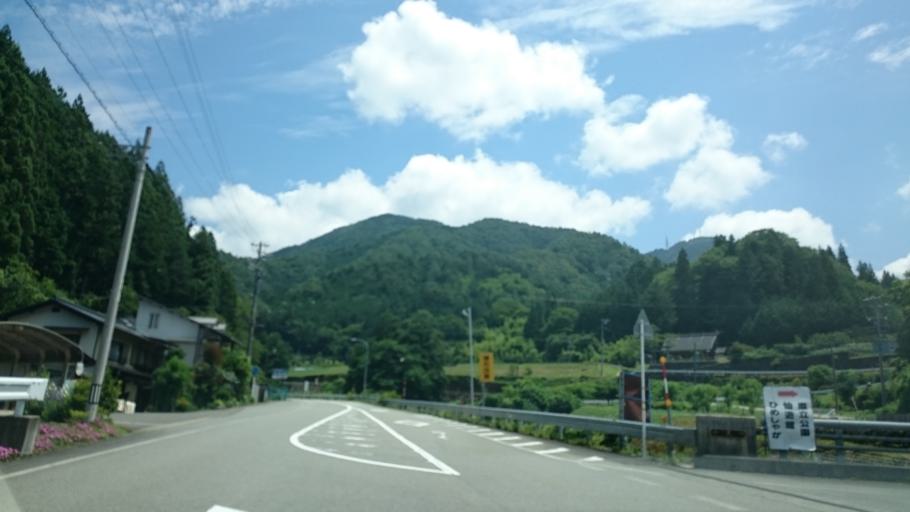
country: JP
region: Gifu
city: Takayama
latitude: 35.9255
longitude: 137.3148
